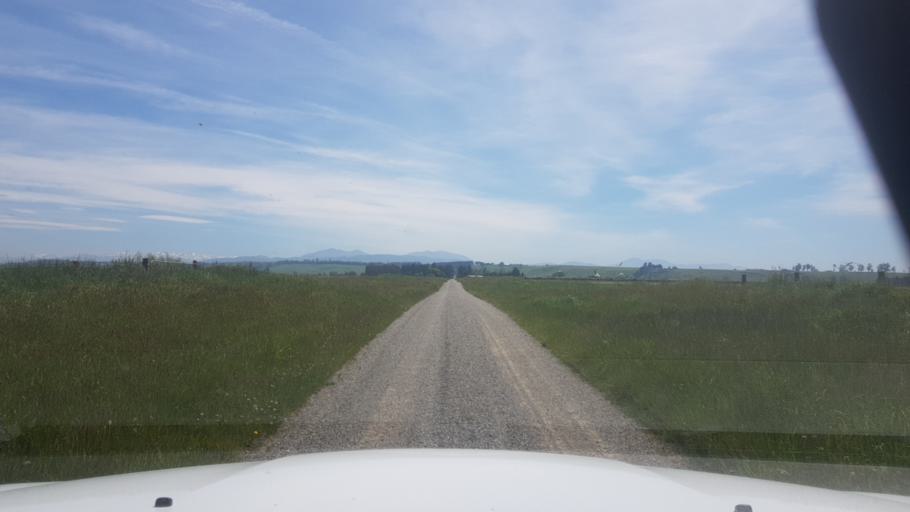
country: NZ
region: Canterbury
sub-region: Timaru District
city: Pleasant Point
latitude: -44.2320
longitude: 171.1670
